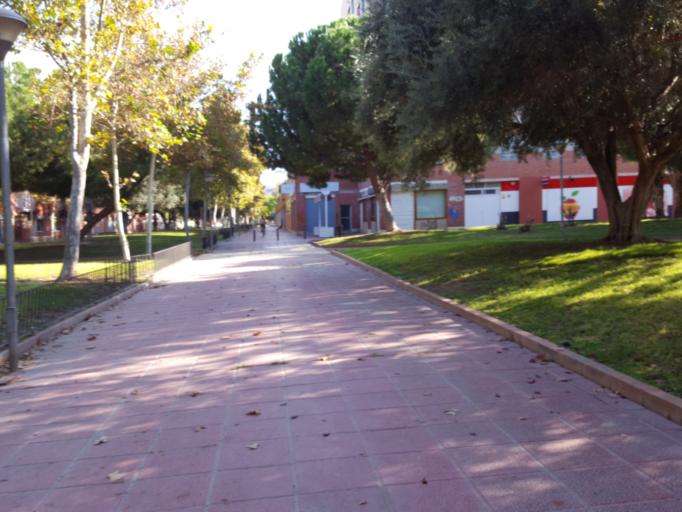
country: ES
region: Murcia
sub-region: Murcia
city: Murcia
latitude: 37.9959
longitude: -1.1246
